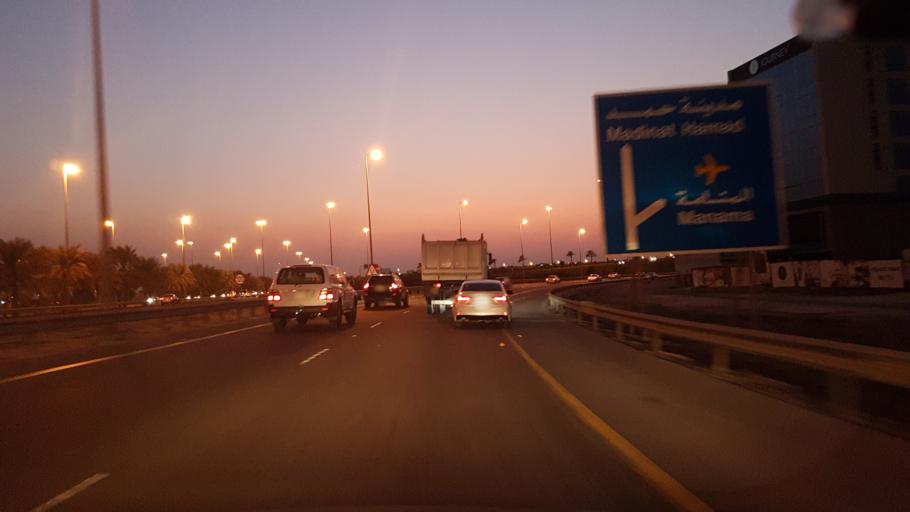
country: BH
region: Northern
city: Madinat `Isa
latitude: 26.1882
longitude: 50.5078
